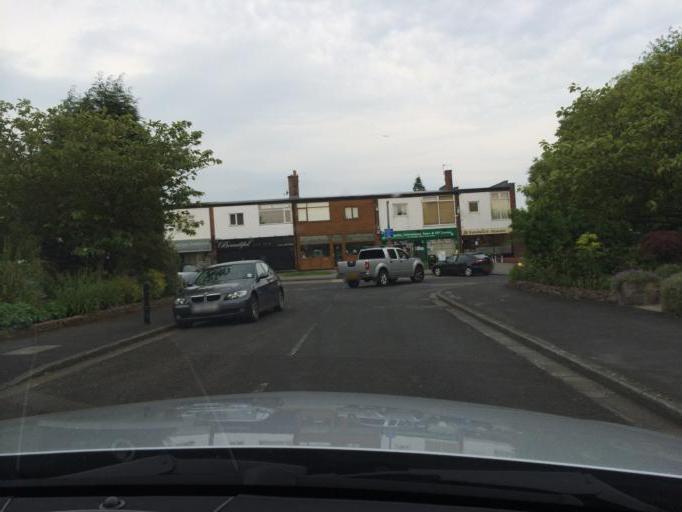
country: GB
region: England
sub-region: Borough of Stockport
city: Hazel Grove
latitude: 53.3721
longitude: -2.1396
